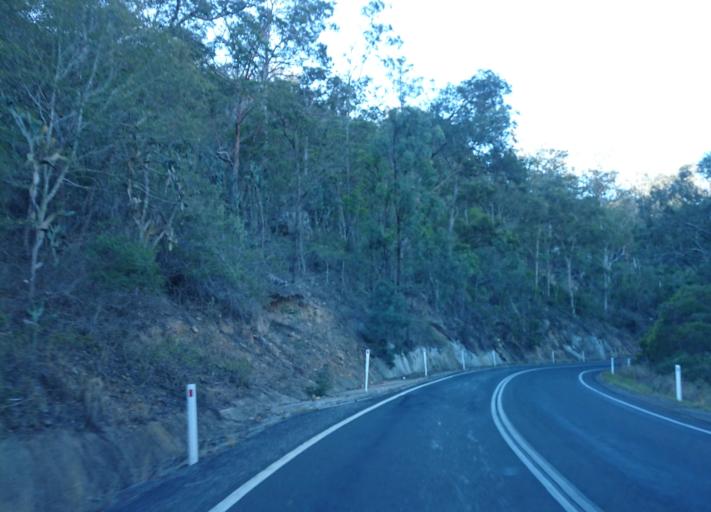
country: AU
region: Queensland
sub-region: Toowoomba
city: Top Camp
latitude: -27.7471
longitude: 152.0893
